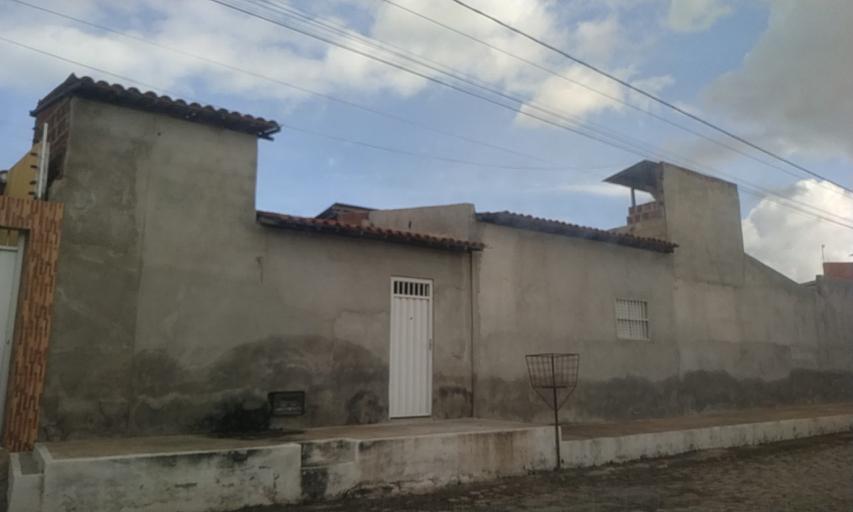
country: BR
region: Rio Grande do Norte
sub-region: Areia Branca
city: Areia Branca
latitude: -4.9530
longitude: -37.1261
